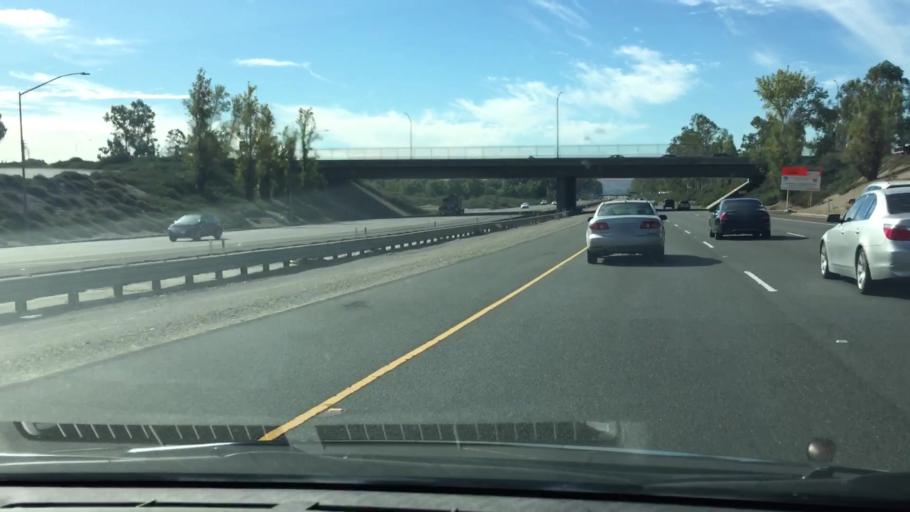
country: US
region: California
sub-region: Orange County
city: Lake Forest
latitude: 33.6980
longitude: -117.7349
